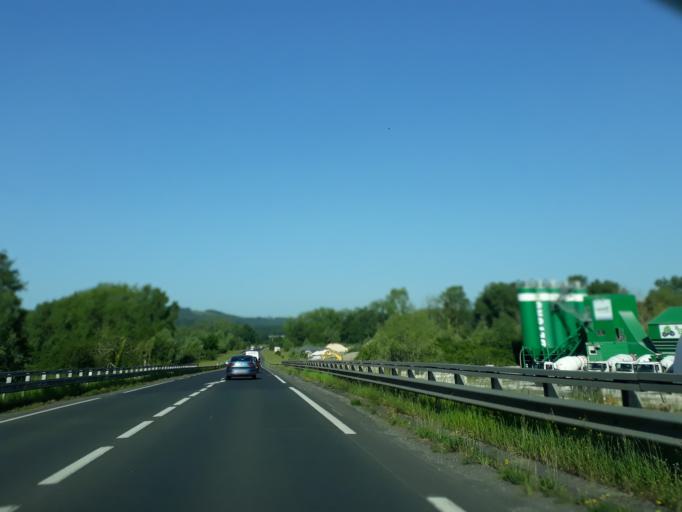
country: FR
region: Limousin
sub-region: Departement de la Correze
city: Saint-Pantaleon-de-Larche
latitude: 45.1275
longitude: 1.4351
